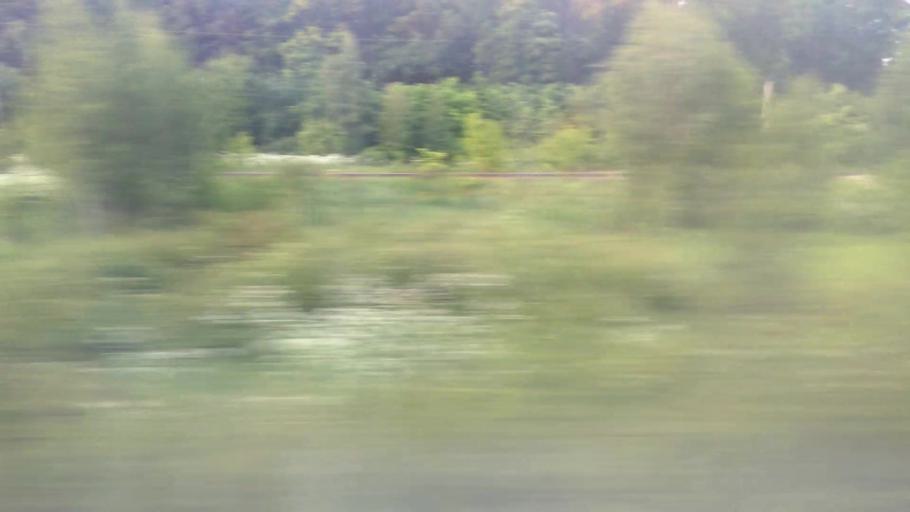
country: RU
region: Moskovskaya
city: Barybino
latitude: 55.3003
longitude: 37.8790
